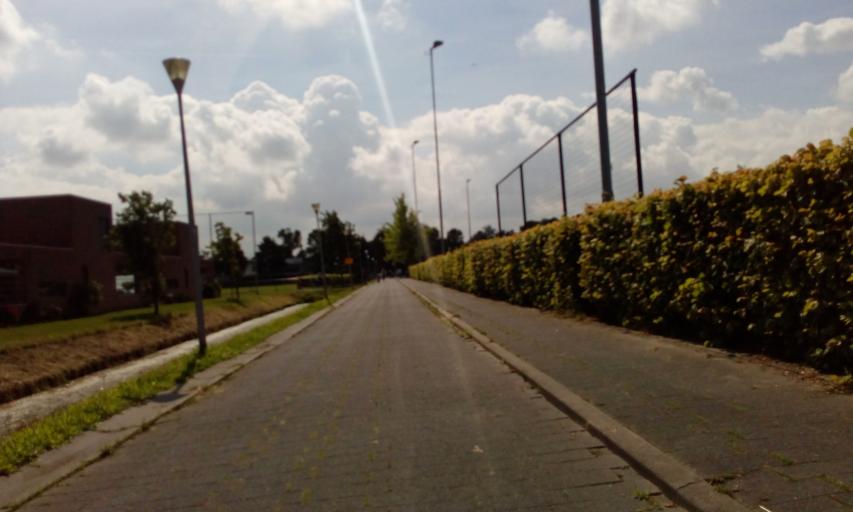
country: NL
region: South Holland
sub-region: Gemeente Den Haag
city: Ypenburg
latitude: 52.0491
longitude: 4.3912
